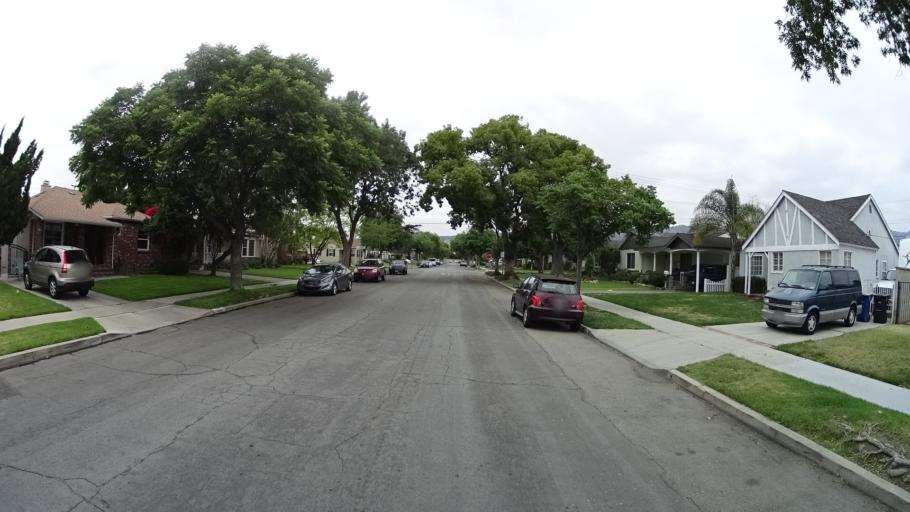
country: US
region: California
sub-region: Los Angeles County
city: Burbank
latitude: 34.1877
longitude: -118.3426
